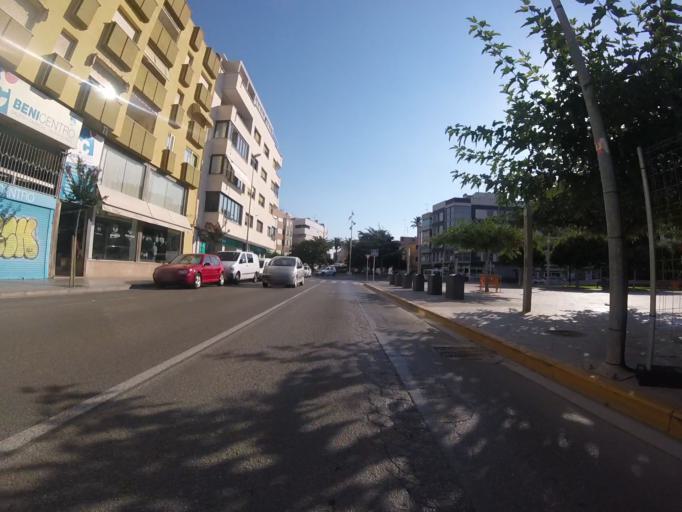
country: ES
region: Valencia
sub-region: Provincia de Castello
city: Benicarlo
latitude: 40.4170
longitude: 0.4238
